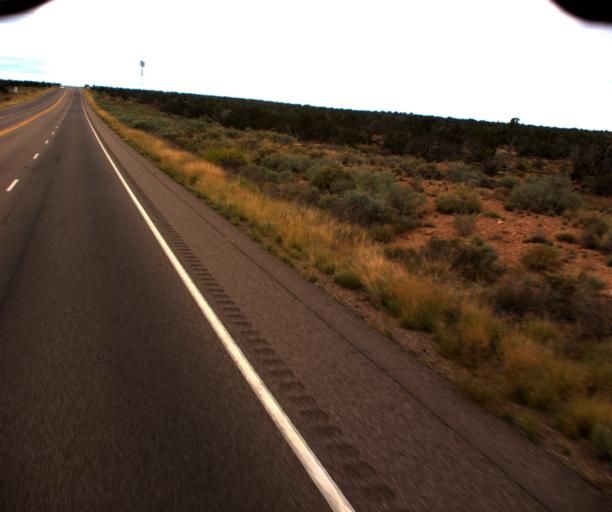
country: US
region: Arizona
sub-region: Navajo County
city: Snowflake
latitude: 34.6413
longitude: -110.0963
